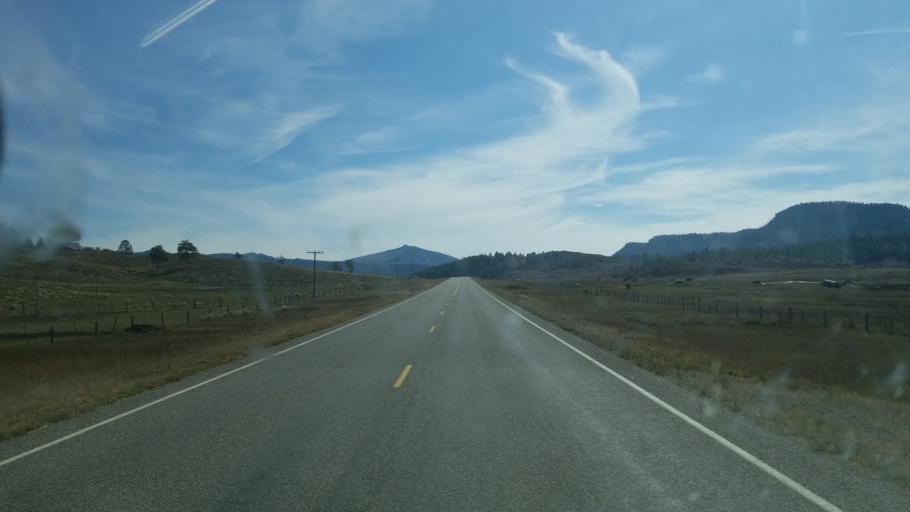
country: US
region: New Mexico
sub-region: Rio Arriba County
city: Dulce
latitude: 37.0263
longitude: -106.8231
